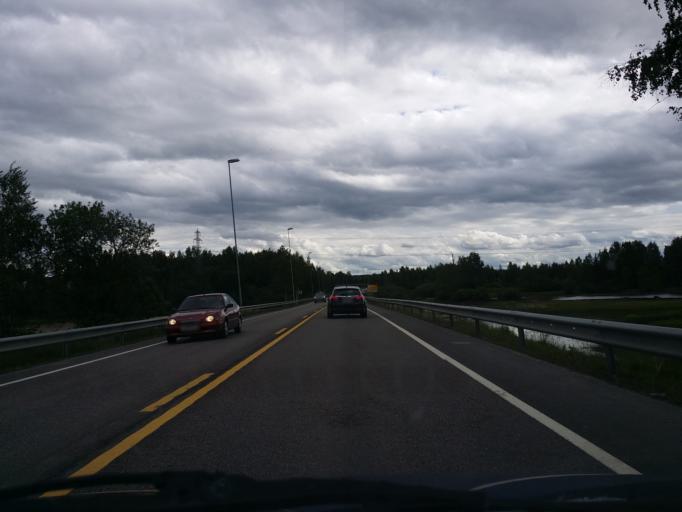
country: NO
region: Hedmark
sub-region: Hamar
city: Hamar
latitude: 60.8038
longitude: 11.1130
